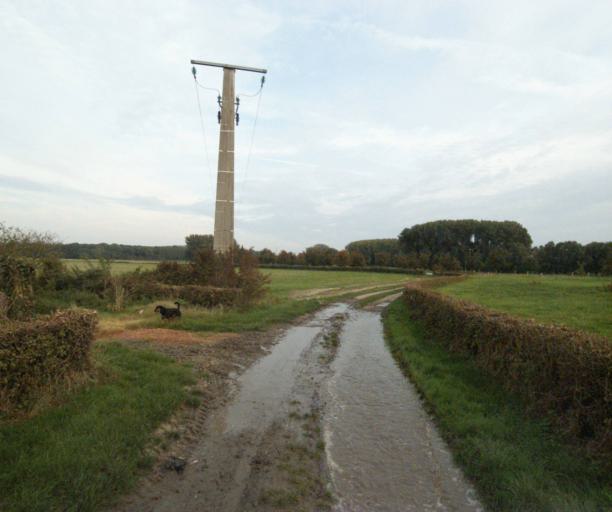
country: FR
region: Nord-Pas-de-Calais
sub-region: Departement du Nord
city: Attiches
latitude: 50.5332
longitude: 3.0556
